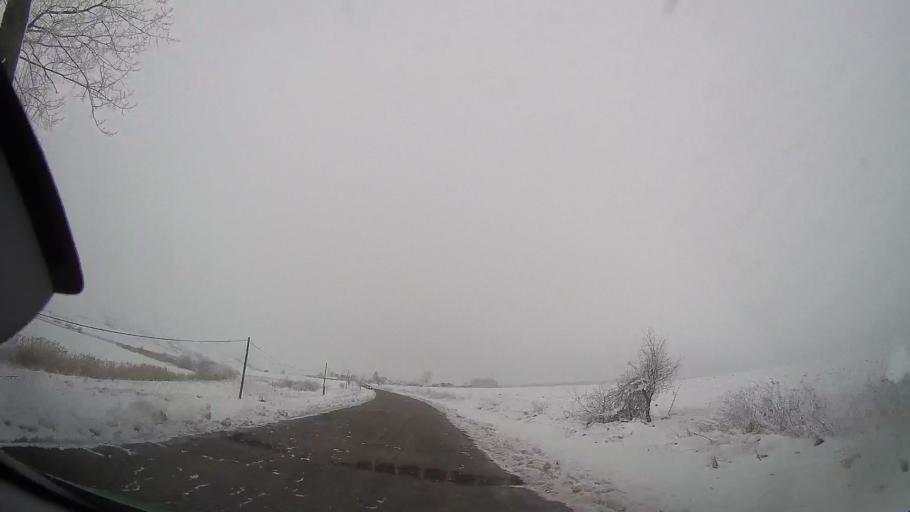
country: RO
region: Neamt
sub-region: Comuna Valea Ursului
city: Chilii
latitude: 46.8548
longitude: 27.0350
